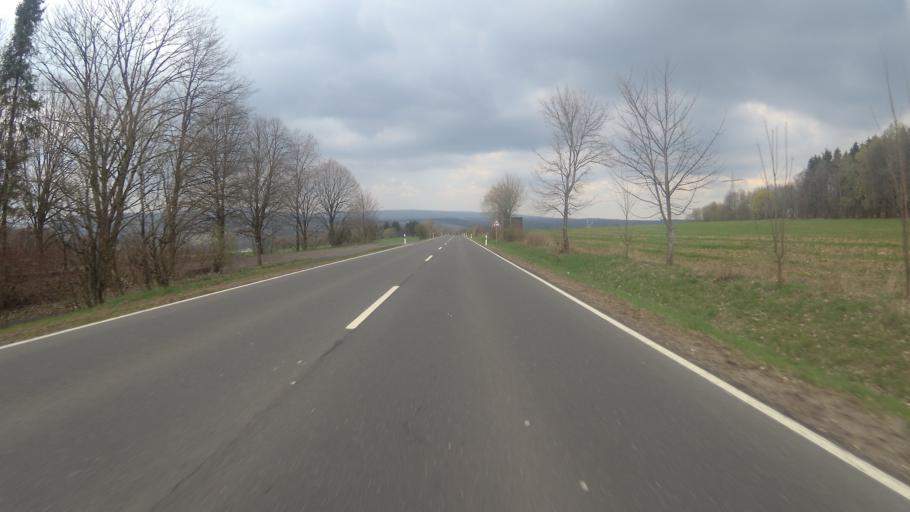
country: DE
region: Rheinland-Pfalz
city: Hermeskeil
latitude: 49.6444
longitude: 6.9486
